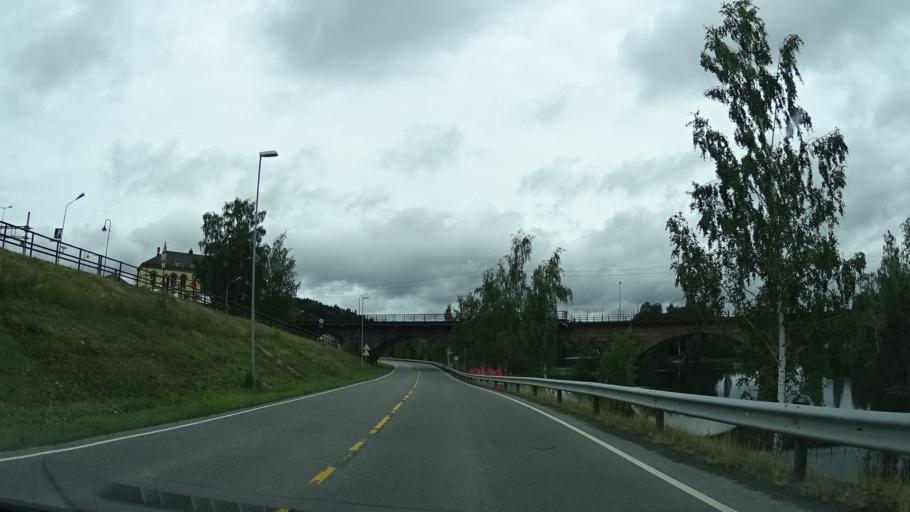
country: NO
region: Buskerud
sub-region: Ringerike
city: Honefoss
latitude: 60.1691
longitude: 10.2515
